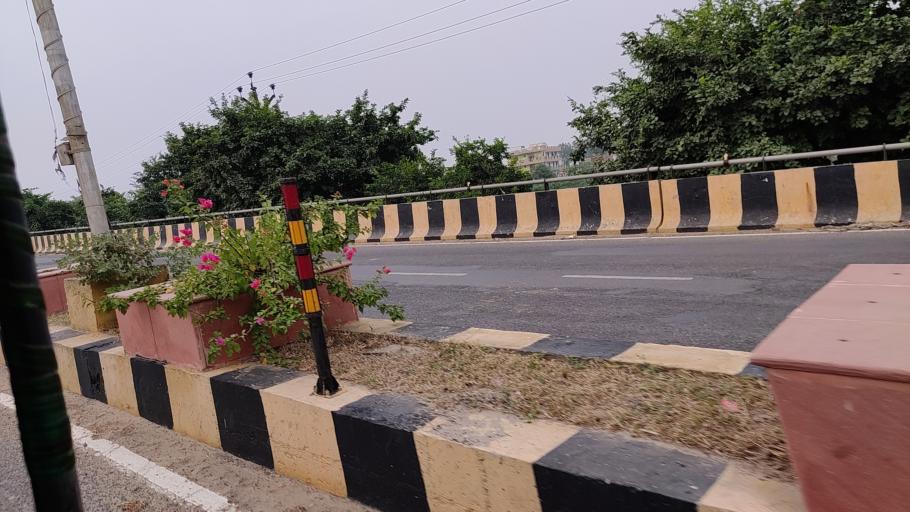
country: IN
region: Uttar Pradesh
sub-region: Mathura
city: Vrindavan
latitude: 27.5625
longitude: 77.6813
